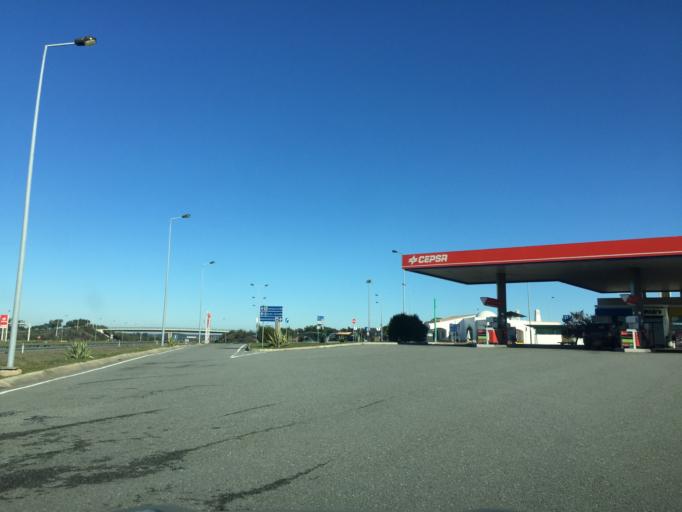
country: PT
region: Beja
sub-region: Almodovar
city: Almodovar
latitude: 37.5355
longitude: -8.1830
